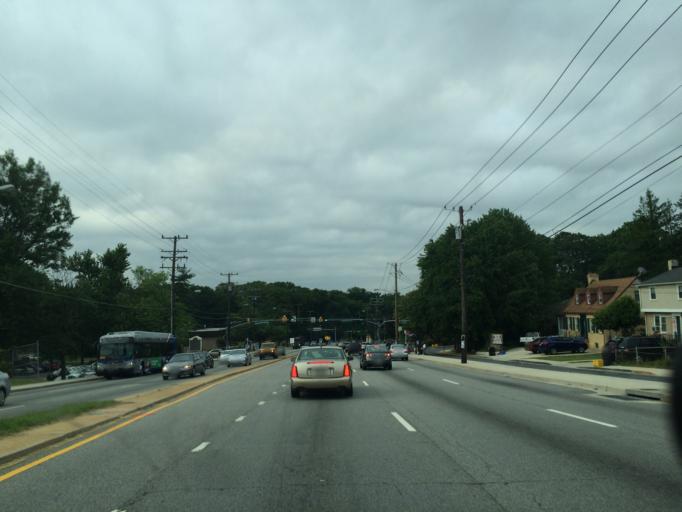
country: US
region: Maryland
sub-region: Prince George's County
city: Langley Park
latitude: 38.9845
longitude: -76.9883
